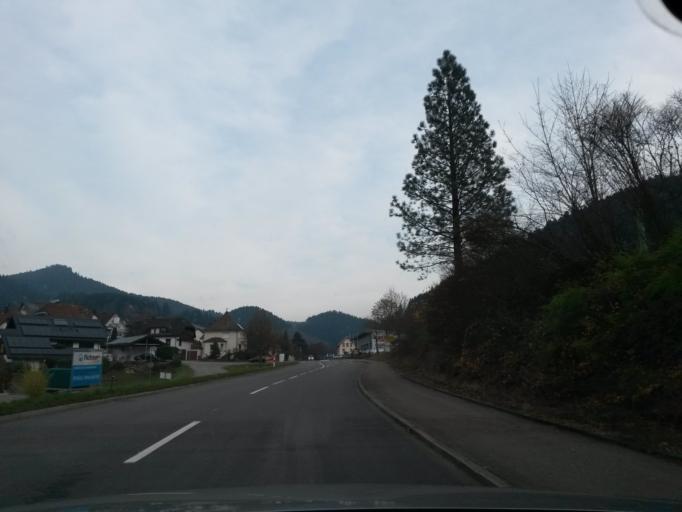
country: DE
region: Baden-Wuerttemberg
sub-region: Freiburg Region
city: Schenkenzell
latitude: 48.3066
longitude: 8.3693
